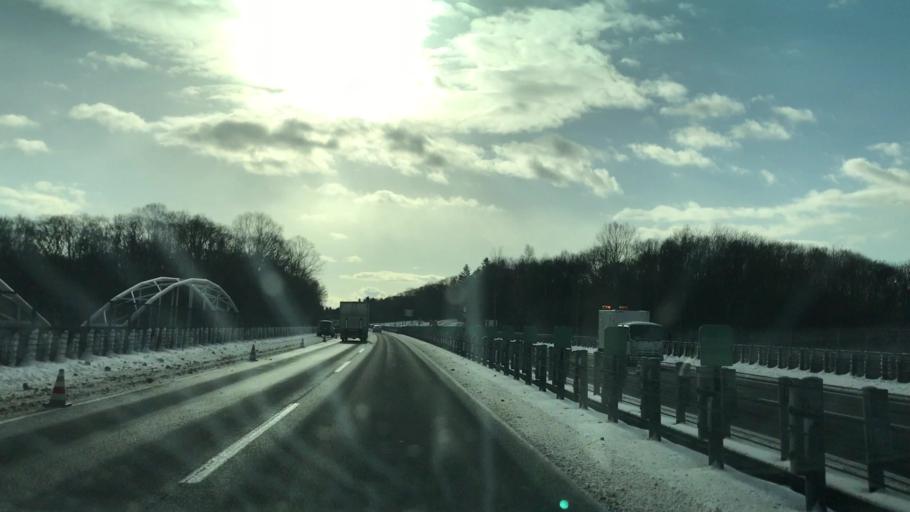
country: JP
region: Hokkaido
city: Chitose
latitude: 42.8625
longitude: 141.5585
